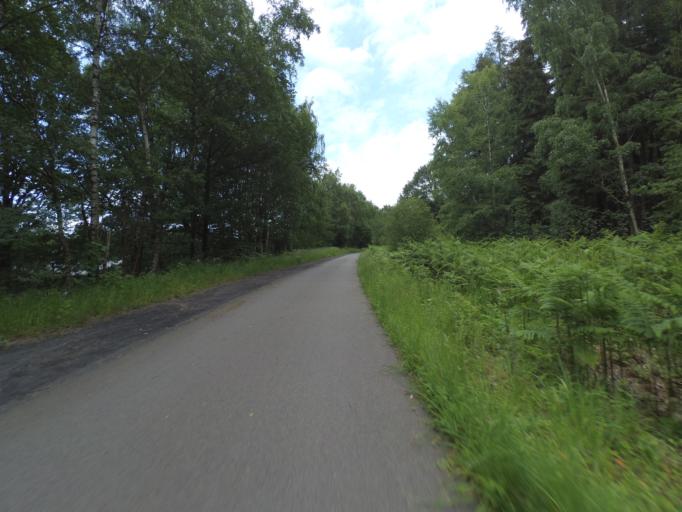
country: BE
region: Wallonia
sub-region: Province de Liege
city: Raeren
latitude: 50.6603
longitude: 6.1211
